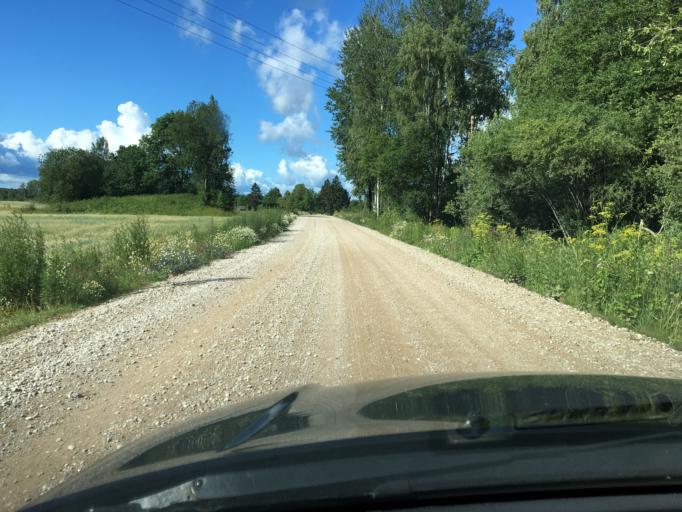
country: LV
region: Kuldigas Rajons
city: Kuldiga
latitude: 56.8405
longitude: 21.9261
